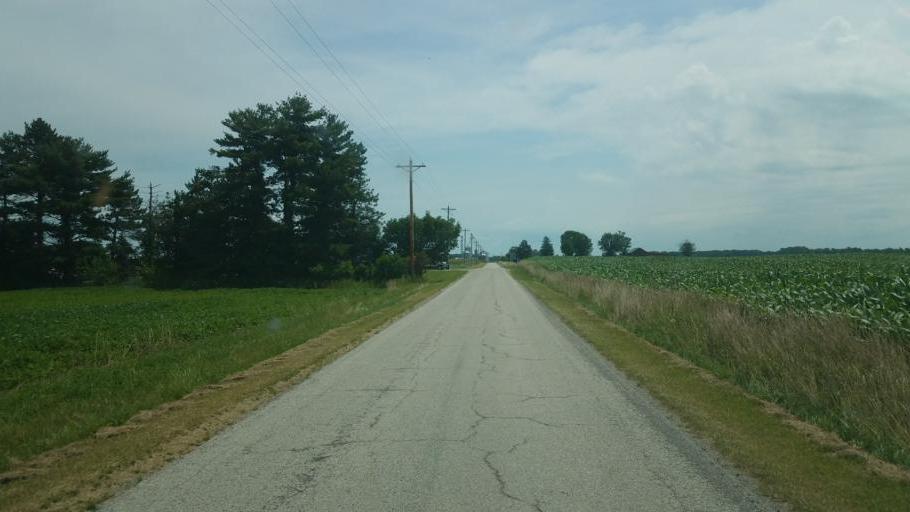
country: US
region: Ohio
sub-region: Crawford County
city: Bucyrus
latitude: 40.8777
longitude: -83.0438
